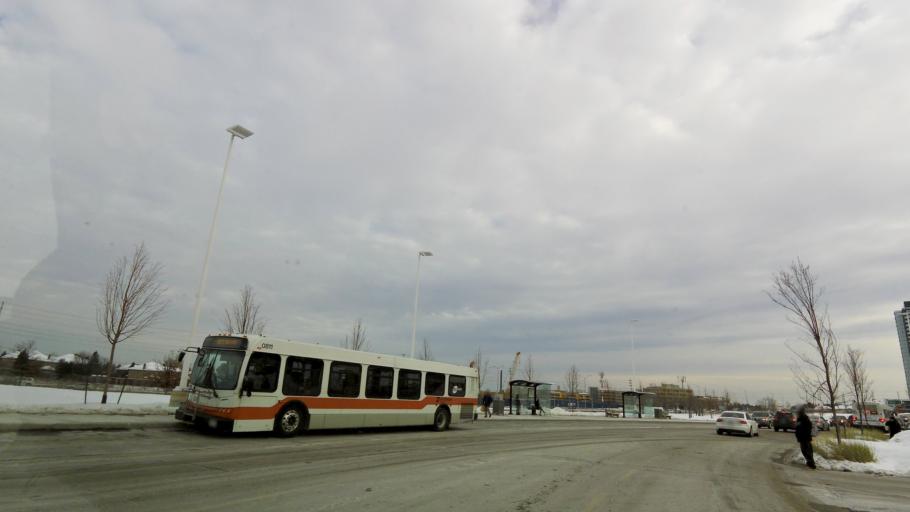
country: CA
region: Ontario
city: Mississauga
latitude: 43.5608
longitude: -79.7113
